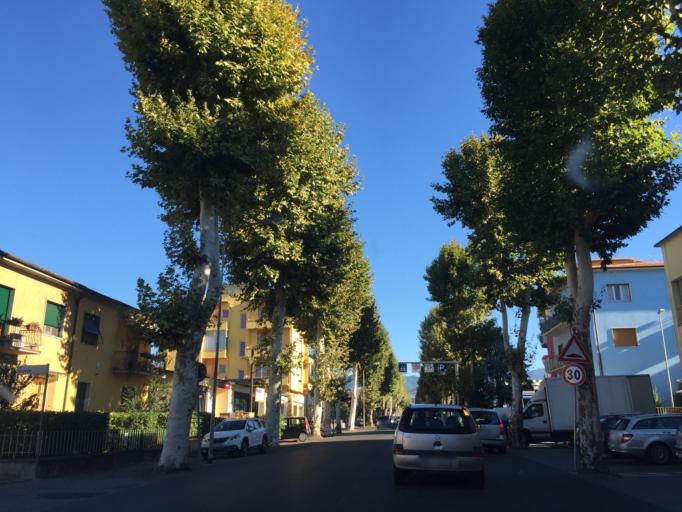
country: IT
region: Tuscany
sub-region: Provincia di Pistoia
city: Pistoia
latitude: 43.9330
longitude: 10.9005
